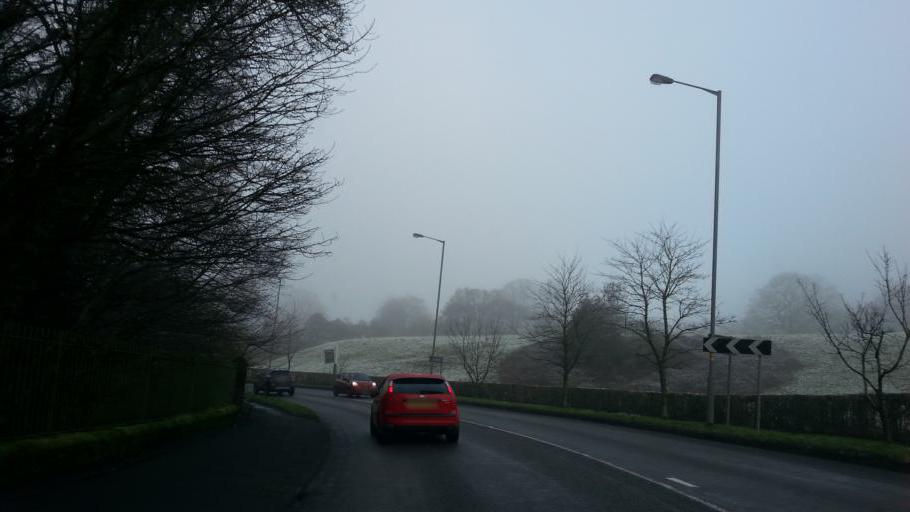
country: GB
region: England
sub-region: Staffordshire
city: Biddulph
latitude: 53.1324
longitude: -2.1659
